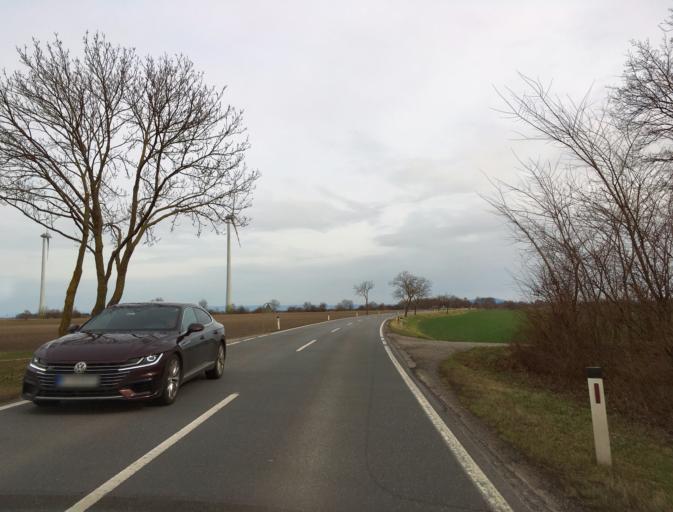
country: AT
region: Lower Austria
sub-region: Politischer Bezirk Ganserndorf
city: Leopoldsdorf im Marchfelde
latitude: 48.2272
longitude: 16.7104
